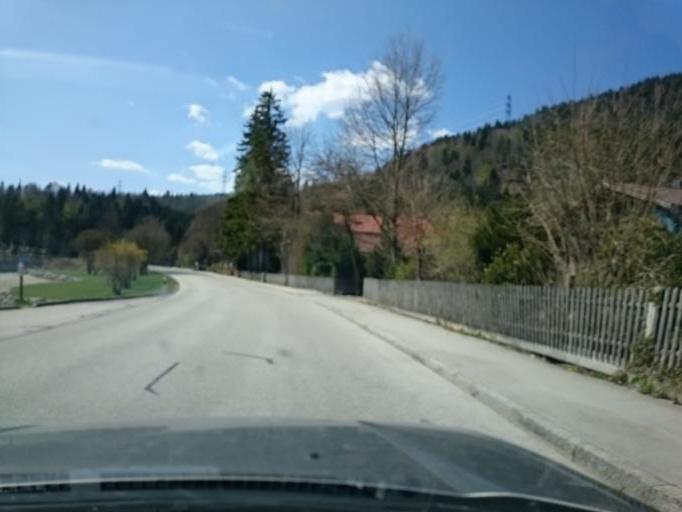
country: DE
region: Bavaria
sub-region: Upper Bavaria
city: Schlehdorf
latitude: 47.5869
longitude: 11.3086
